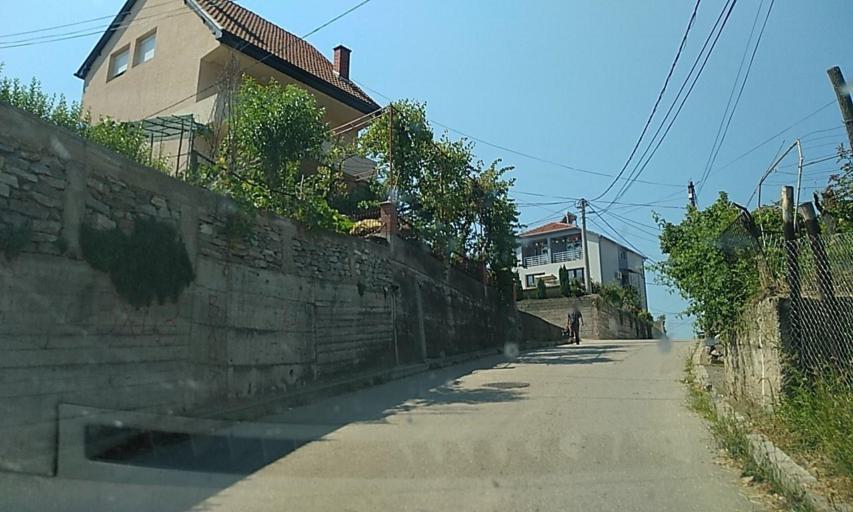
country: RS
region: Central Serbia
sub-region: Pcinjski Okrug
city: Vladicin Han
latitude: 42.7064
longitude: 22.0543
